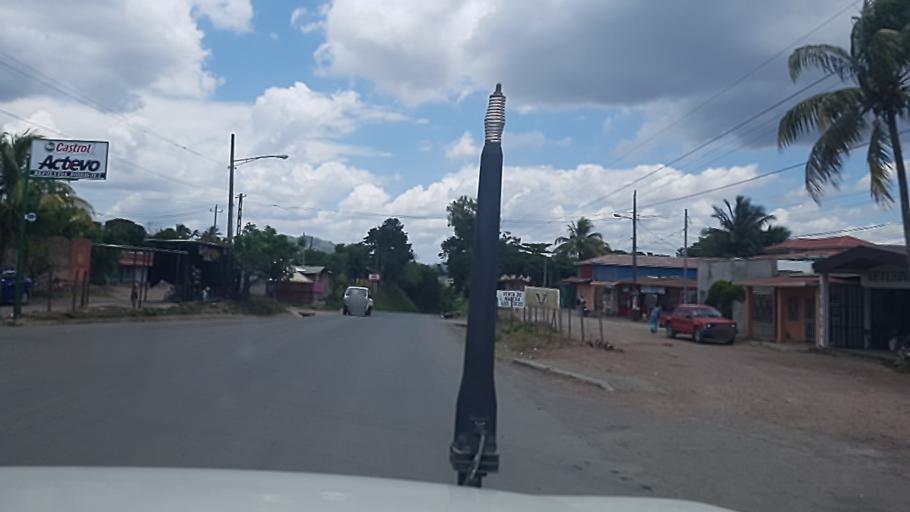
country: NI
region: Chontales
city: Santo Tomas
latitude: 12.0655
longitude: -85.0904
